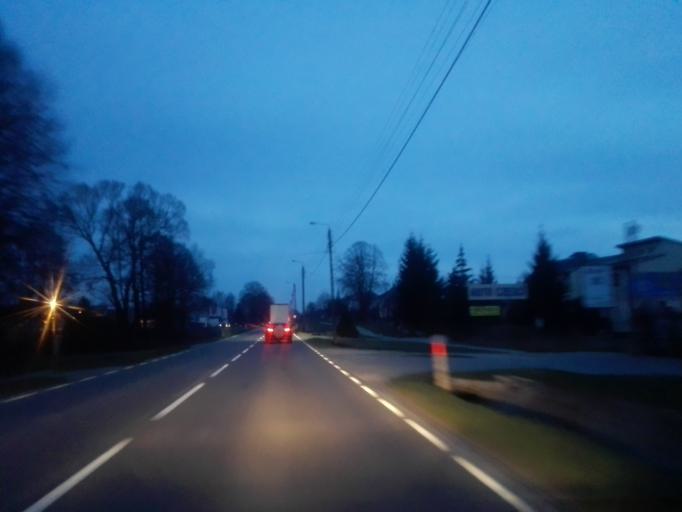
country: PL
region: Podlasie
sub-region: Lomza
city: Lomza
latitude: 53.1437
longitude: 22.0451
